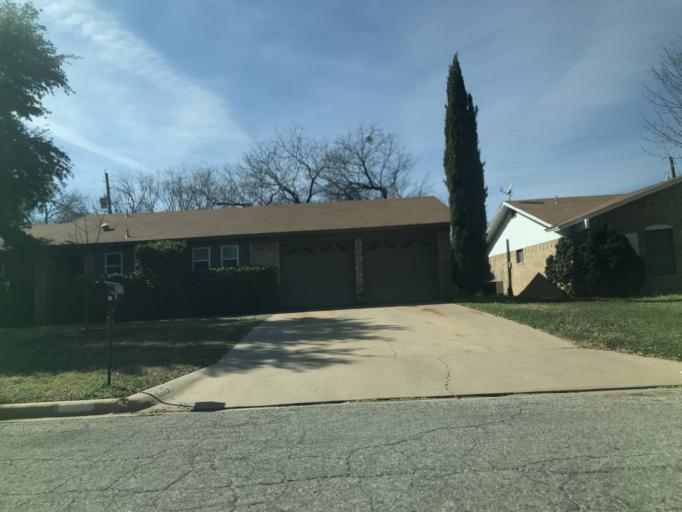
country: US
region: Texas
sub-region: Tom Green County
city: San Angelo
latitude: 31.4345
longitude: -100.4879
